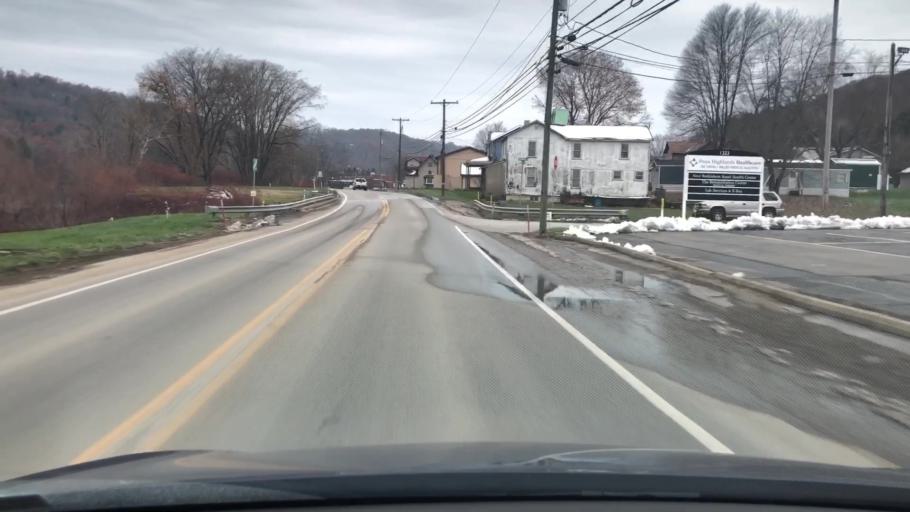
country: US
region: Pennsylvania
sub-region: Clarion County
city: Clarion
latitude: 41.0075
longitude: -79.3126
